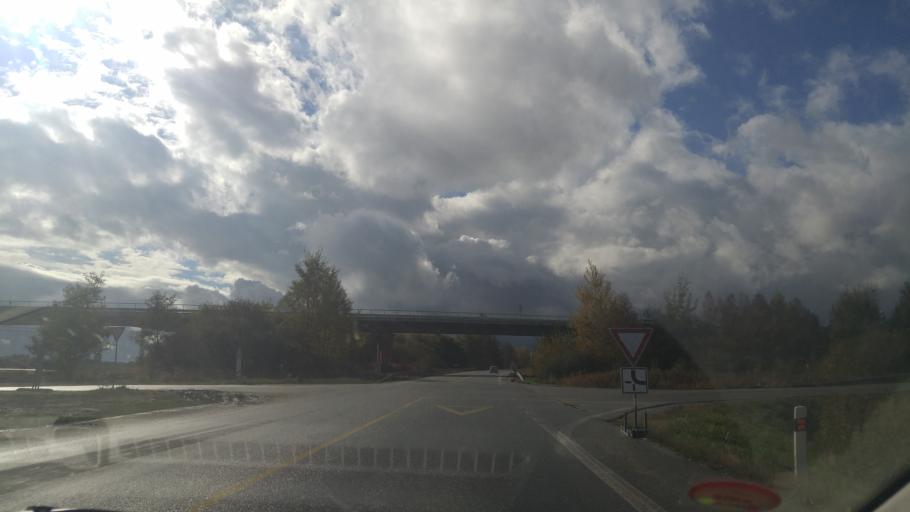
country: CZ
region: Jihocesky
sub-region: Okres Tabor
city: Veseli nad Luznici
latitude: 49.1732
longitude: 14.6818
